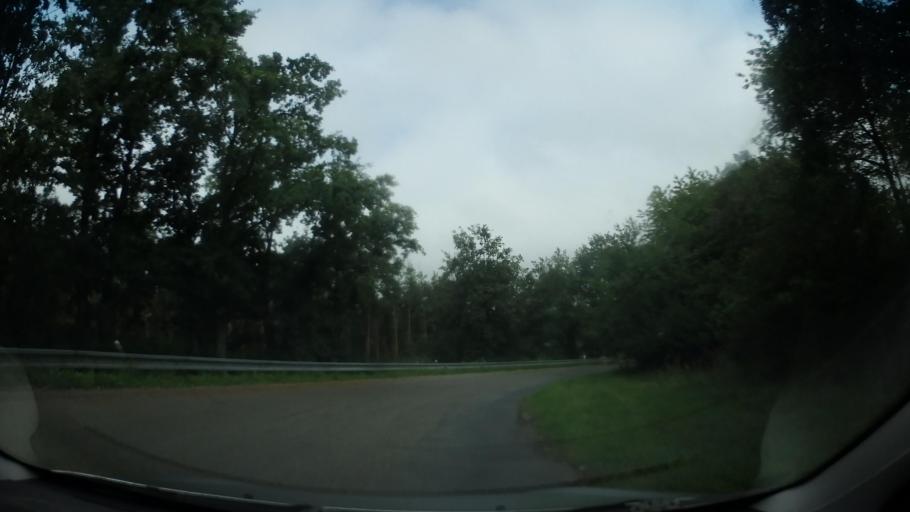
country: CZ
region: Central Bohemia
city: Sedlcany
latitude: 49.7081
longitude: 14.4256
